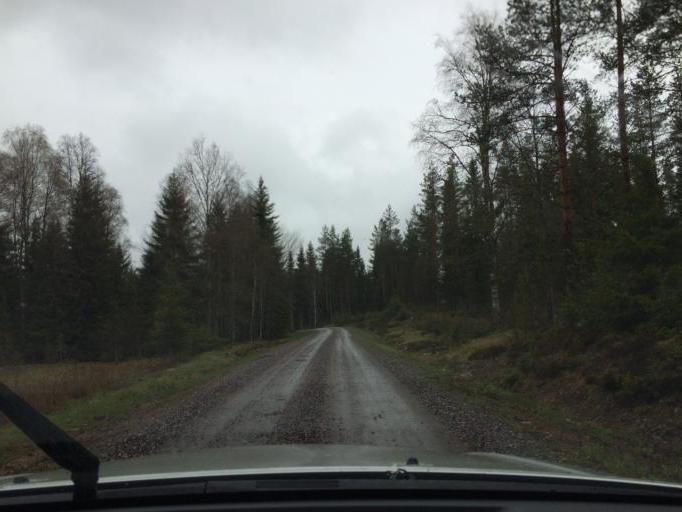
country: SE
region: OErebro
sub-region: Hallefors Kommun
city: Haellefors
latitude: 60.0386
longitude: 14.5274
